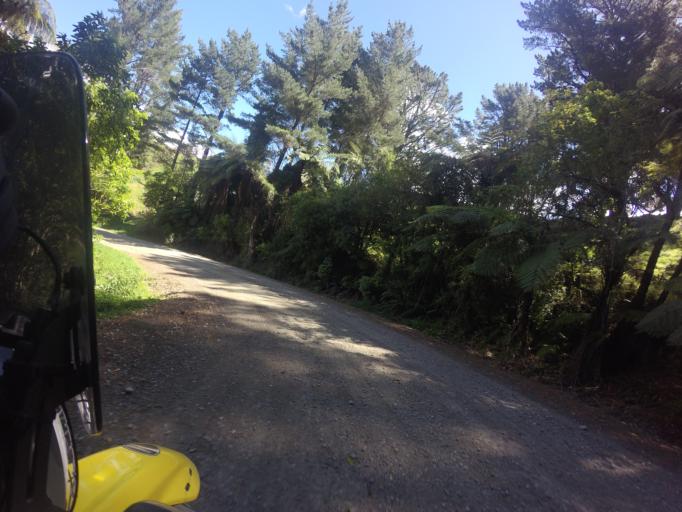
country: NZ
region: Hawke's Bay
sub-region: Wairoa District
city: Wairoa
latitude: -38.9775
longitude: 177.7034
